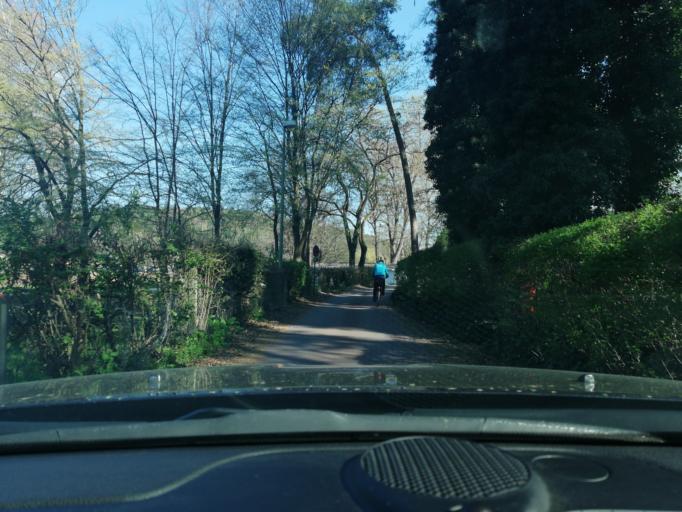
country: DE
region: Bavaria
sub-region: Regierungsbezirk Mittelfranken
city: Hessdorf
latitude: 49.6299
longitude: 10.9512
